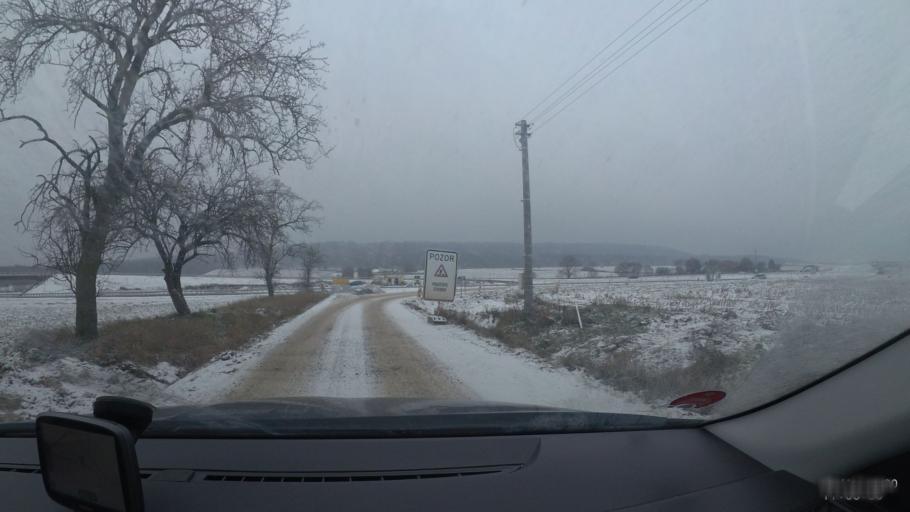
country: CZ
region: Central Bohemia
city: Revnicov
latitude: 50.1779
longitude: 13.8103
